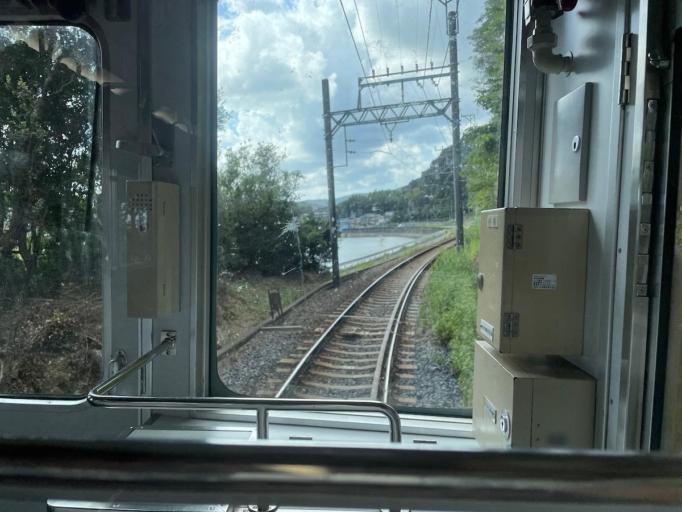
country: JP
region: Mie
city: Toba
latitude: 34.4603
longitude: 136.8413
